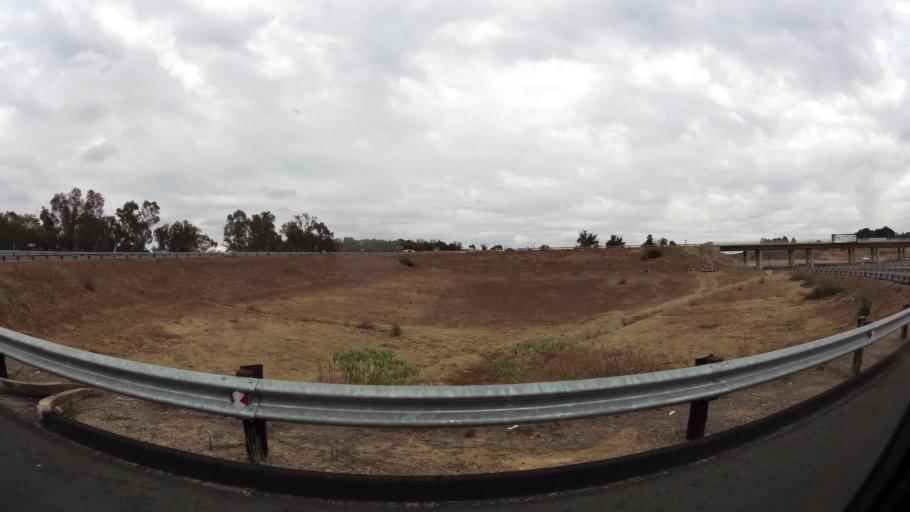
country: ZA
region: Gauteng
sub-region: West Rand District Municipality
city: Muldersdriseloop
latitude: -26.0202
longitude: 27.8622
